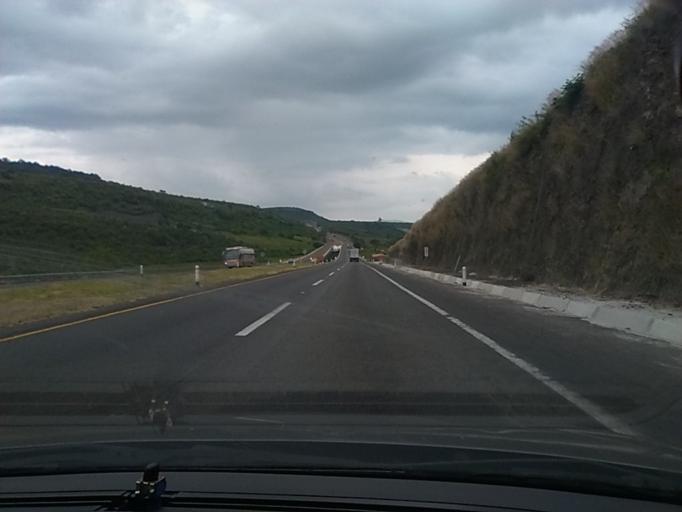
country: MX
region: Jalisco
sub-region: Zapotlan del Rey
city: Zapotlan del Rey
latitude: 20.4952
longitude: -102.9458
